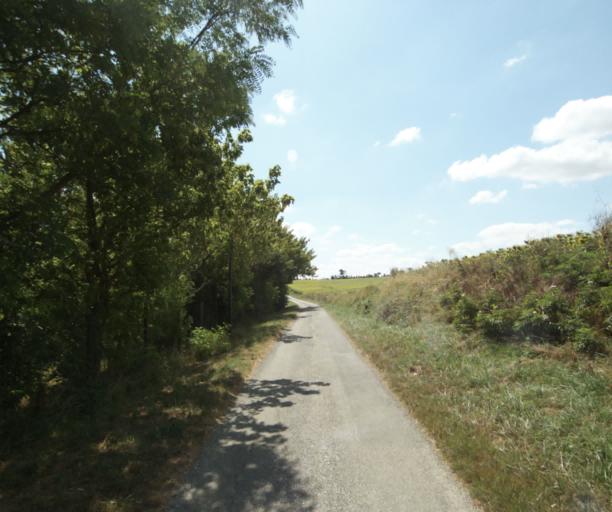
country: FR
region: Midi-Pyrenees
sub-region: Departement de la Haute-Garonne
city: Saint-Felix-Lauragais
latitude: 43.4681
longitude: 1.8394
